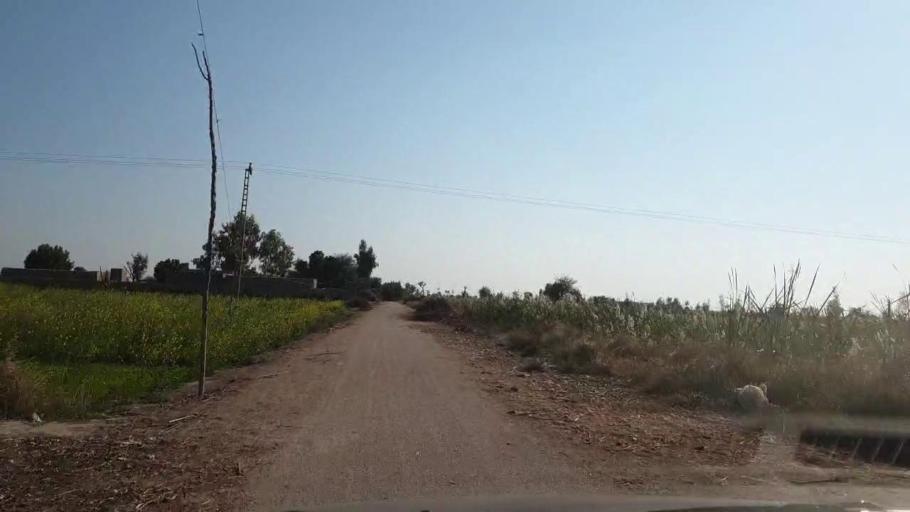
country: PK
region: Sindh
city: Khadro
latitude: 26.1531
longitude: 68.7690
